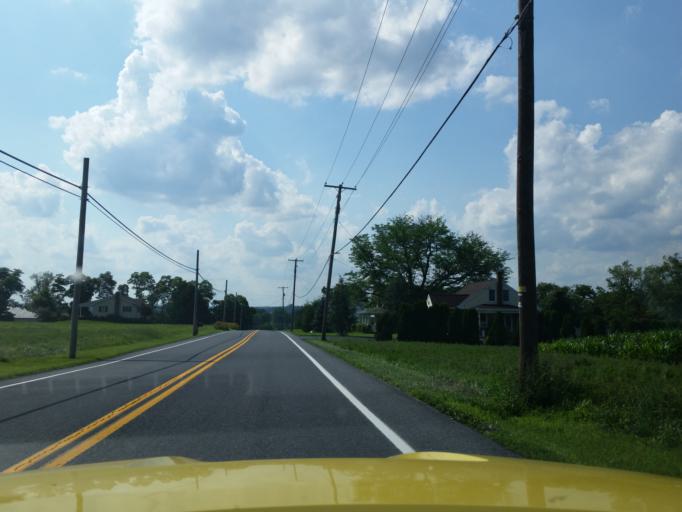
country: US
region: Pennsylvania
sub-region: Lancaster County
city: Manheim
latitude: 40.1832
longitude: -76.4647
